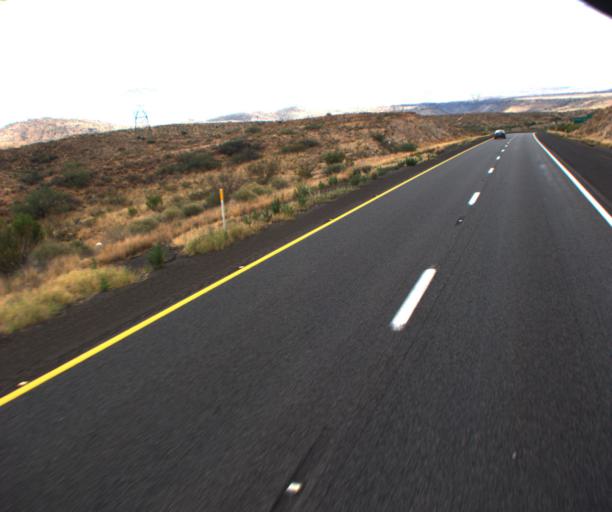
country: US
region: Arizona
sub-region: Yavapai County
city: Cordes Lakes
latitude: 34.2571
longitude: -112.1158
